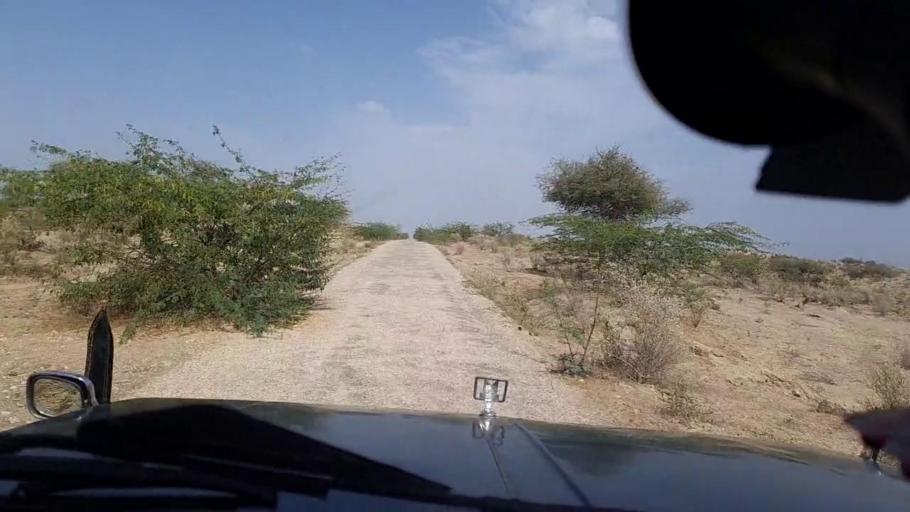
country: PK
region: Sindh
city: Diplo
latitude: 24.4272
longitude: 69.4185
